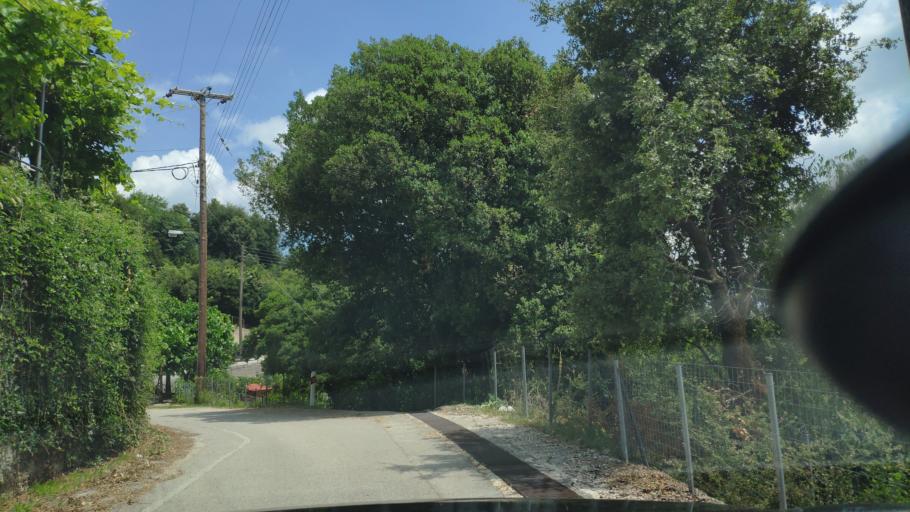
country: GR
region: Epirus
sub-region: Nomos Artas
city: Agios Dimitrios
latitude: 39.3247
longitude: 20.9974
